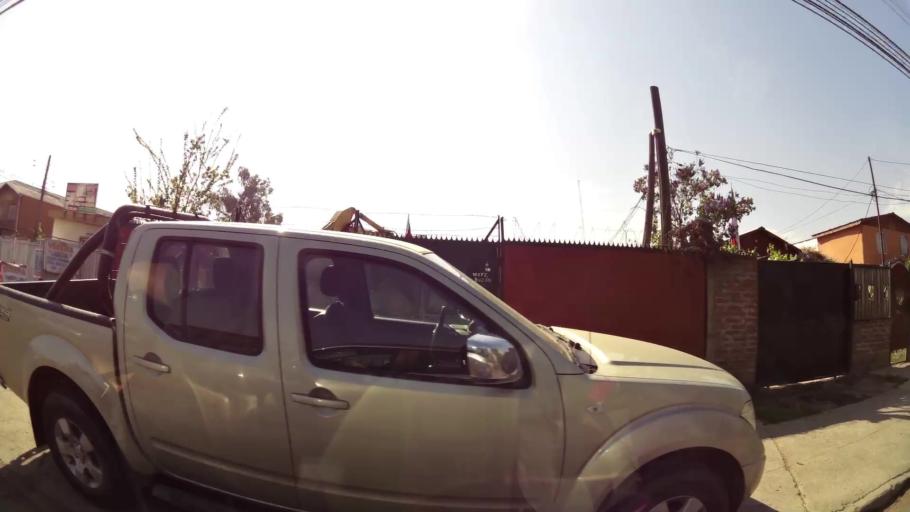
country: CL
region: Santiago Metropolitan
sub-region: Provincia de Santiago
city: La Pintana
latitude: -33.5523
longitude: -70.5926
